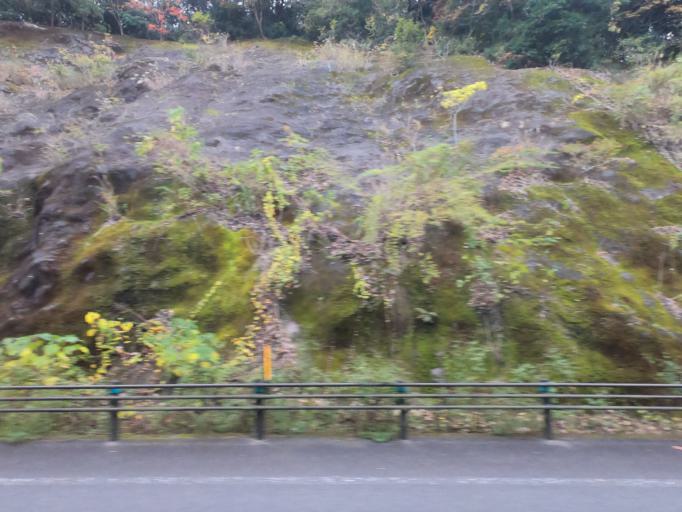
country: JP
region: Kumamoto
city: Minamata
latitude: 32.2606
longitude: 130.5091
